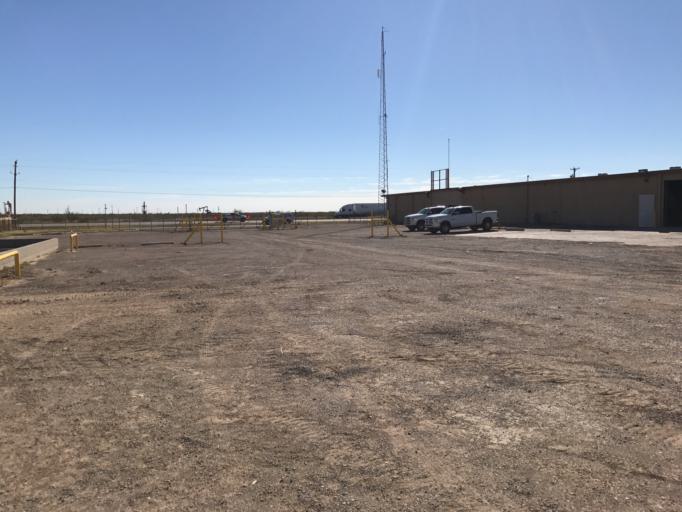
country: US
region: Texas
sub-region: Ector County
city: Odessa
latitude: 31.8990
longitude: -102.2423
